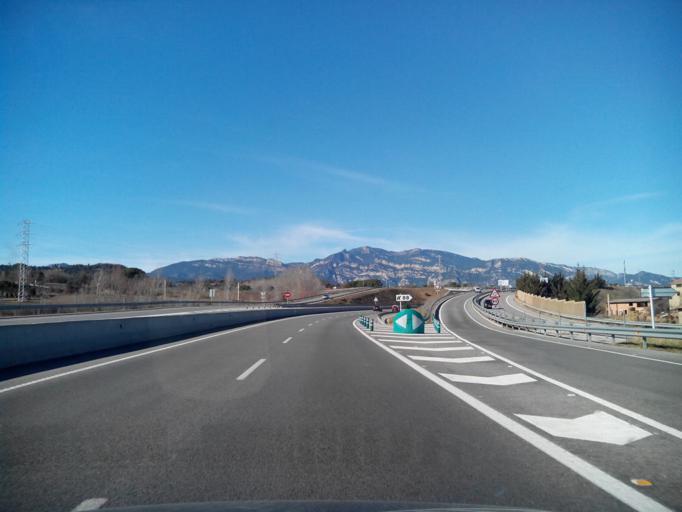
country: ES
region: Catalonia
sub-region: Provincia de Barcelona
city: Gironella
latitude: 42.0293
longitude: 1.8753
